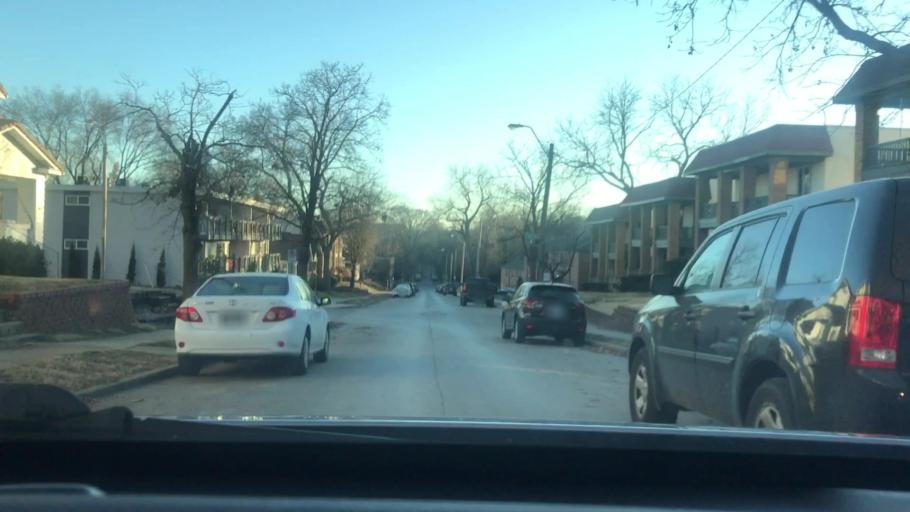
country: US
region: Kansas
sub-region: Johnson County
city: Westwood
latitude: 39.0485
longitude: -94.6006
